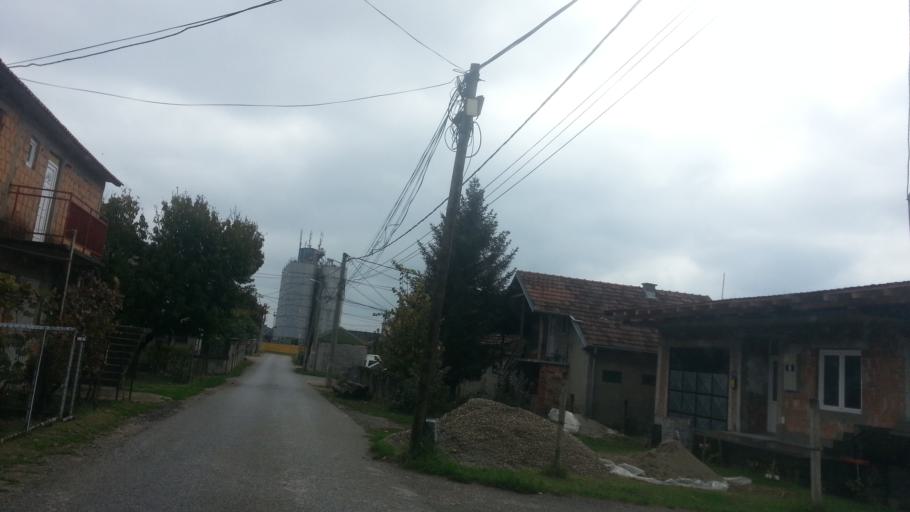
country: RS
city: Novi Banovci
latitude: 44.9119
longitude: 20.2894
